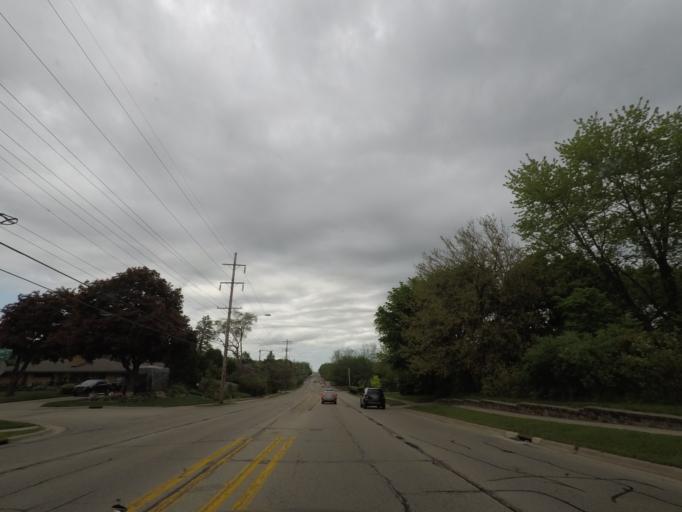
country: US
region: Illinois
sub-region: Winnebago County
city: Loves Park
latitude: 42.2923
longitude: -89.0291
